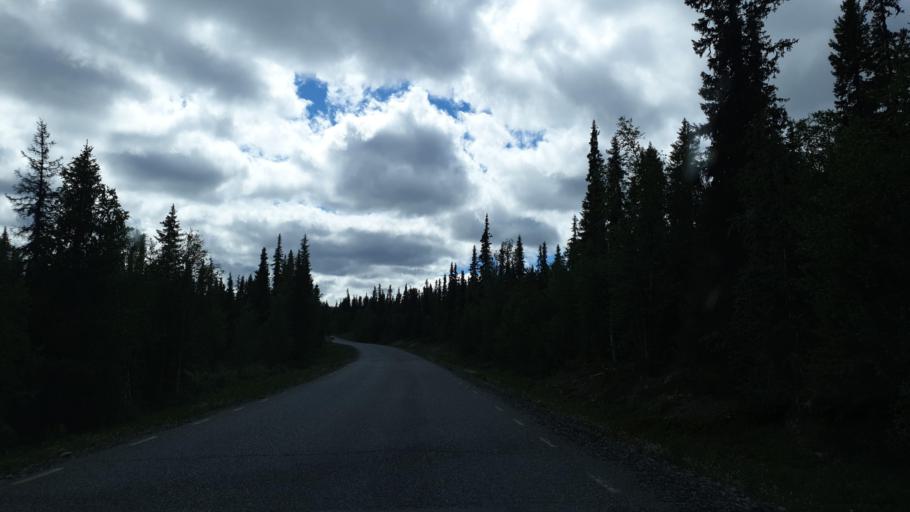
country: SE
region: Vaesterbotten
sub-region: Vilhelmina Kommun
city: Sjoberg
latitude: 65.1314
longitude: 15.8759
